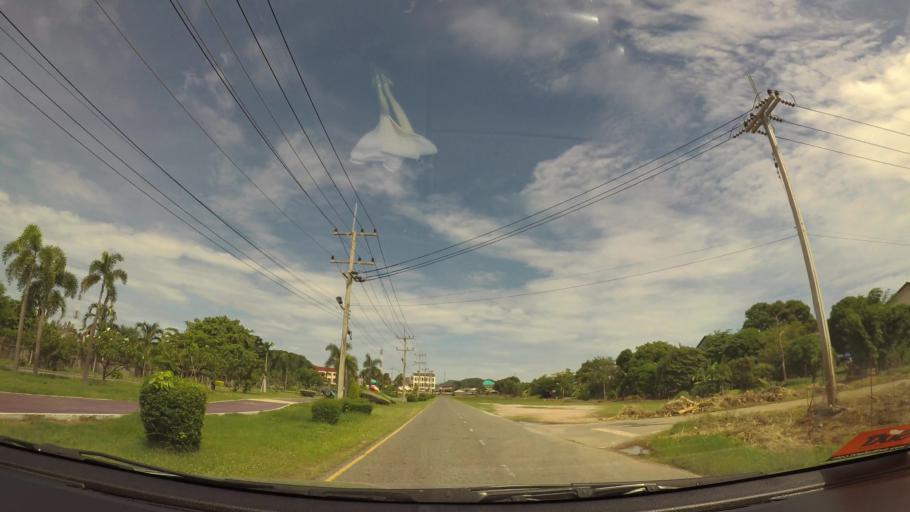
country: TH
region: Chon Buri
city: Sattahip
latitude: 12.6688
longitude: 100.9053
